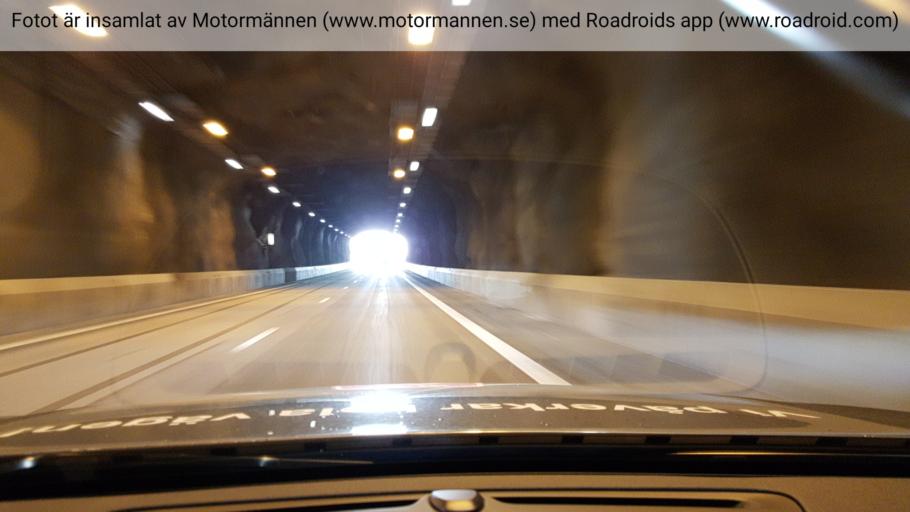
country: SE
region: Uppsala
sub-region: Enkopings Kommun
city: Hummelsta
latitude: 59.6371
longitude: 16.8741
